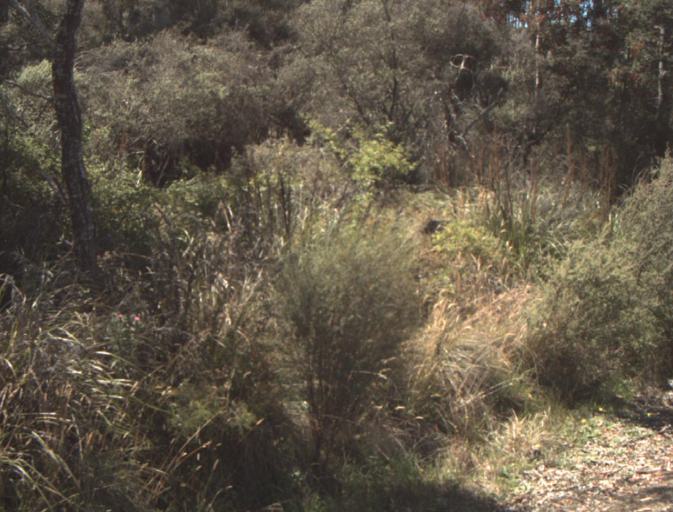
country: AU
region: Tasmania
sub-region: Launceston
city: Newstead
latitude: -41.3822
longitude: 147.3123
